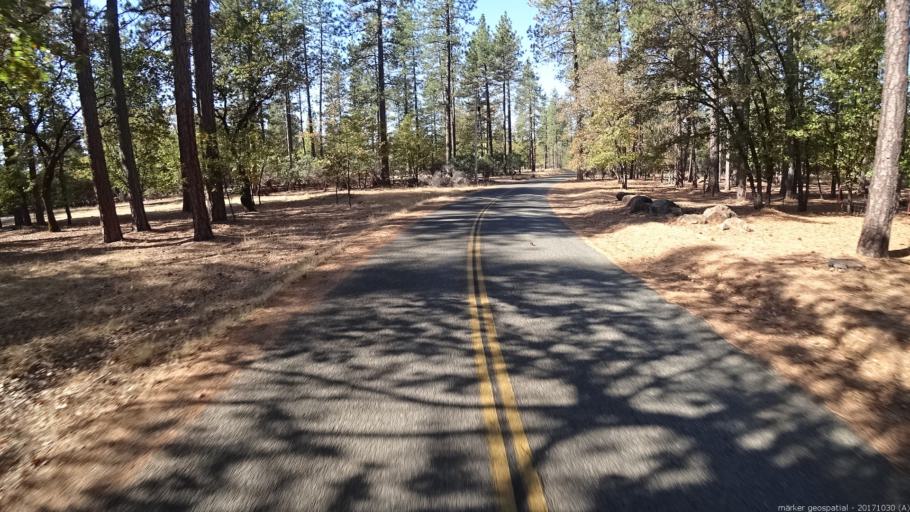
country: US
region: California
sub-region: Shasta County
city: Shingletown
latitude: 40.6009
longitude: -121.9675
